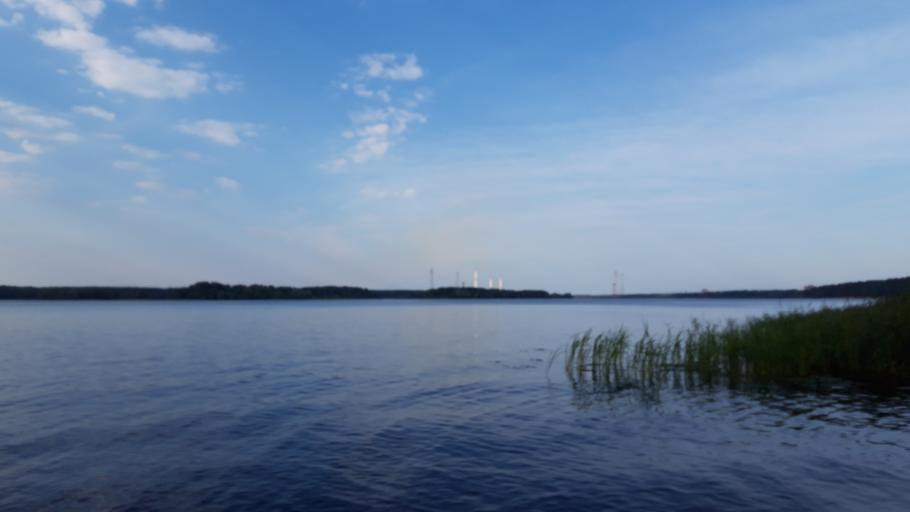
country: RU
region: Tverskaya
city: Konakovo
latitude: 56.6962
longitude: 36.7247
